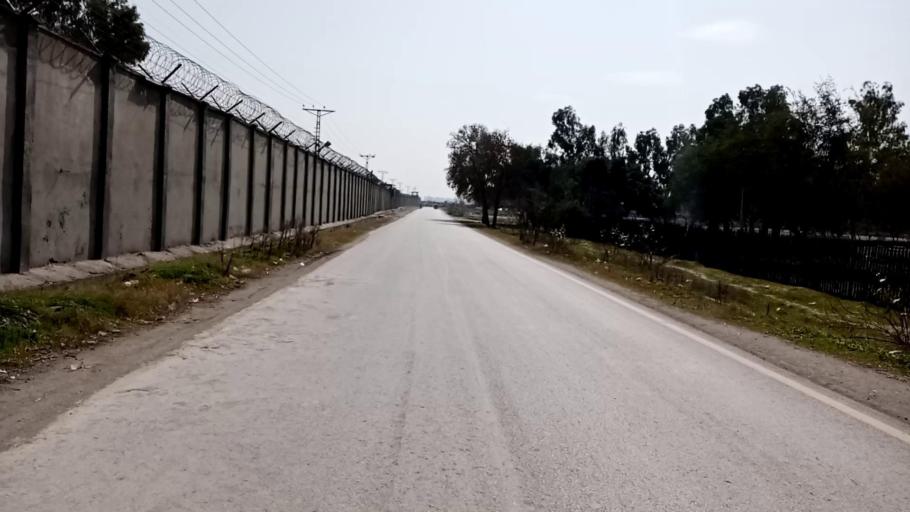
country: PK
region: Khyber Pakhtunkhwa
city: Peshawar
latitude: 33.9904
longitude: 71.5113
